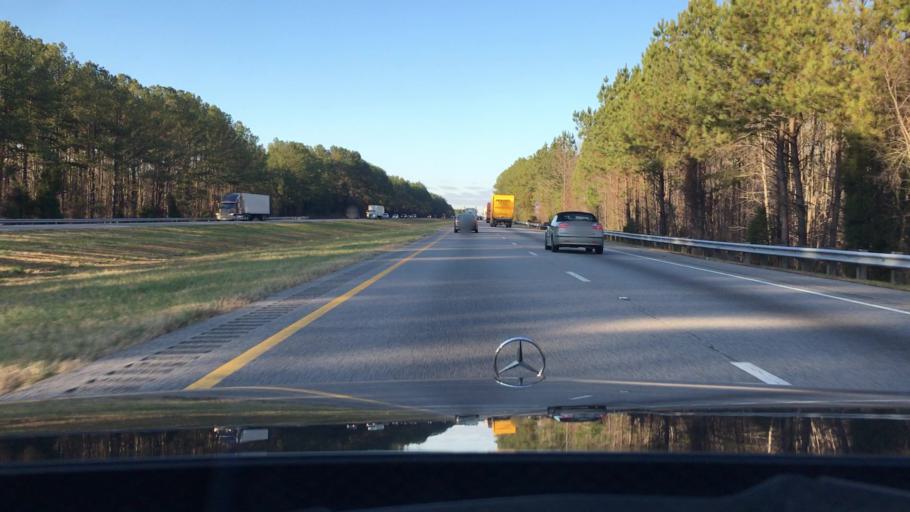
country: US
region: South Carolina
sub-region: Chester County
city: Eureka Mill
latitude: 34.7330
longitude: -81.0341
